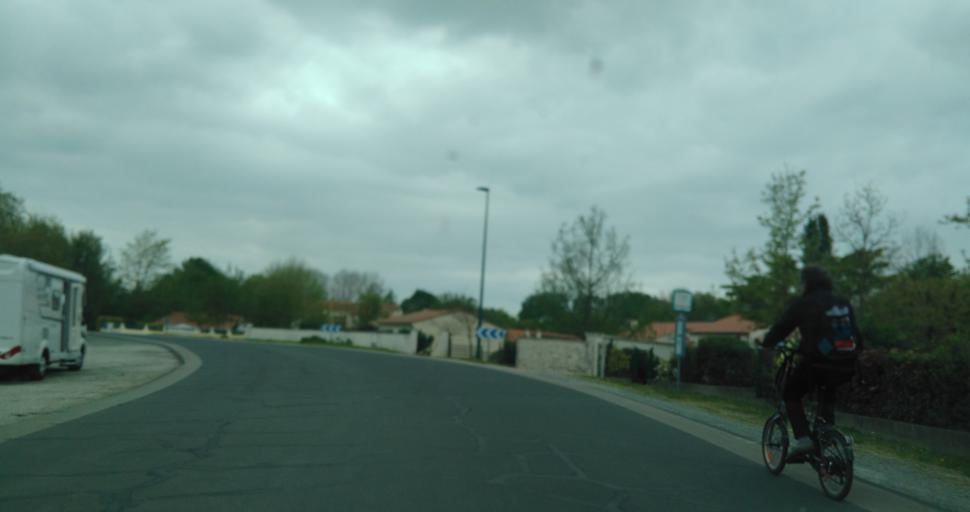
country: FR
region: Poitou-Charentes
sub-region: Departement des Deux-Sevres
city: Coulon
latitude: 46.3149
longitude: -0.6076
